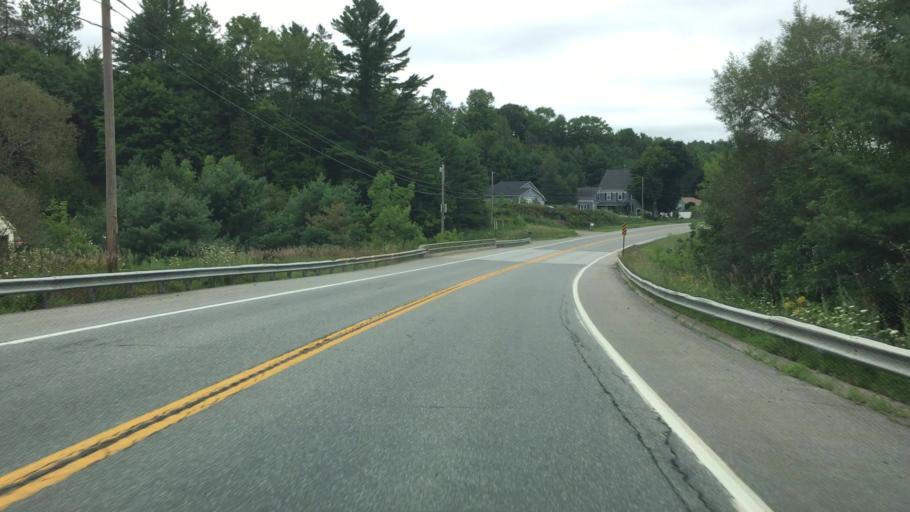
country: US
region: Maine
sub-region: Penobscot County
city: Orrington
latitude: 44.6938
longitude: -68.8478
